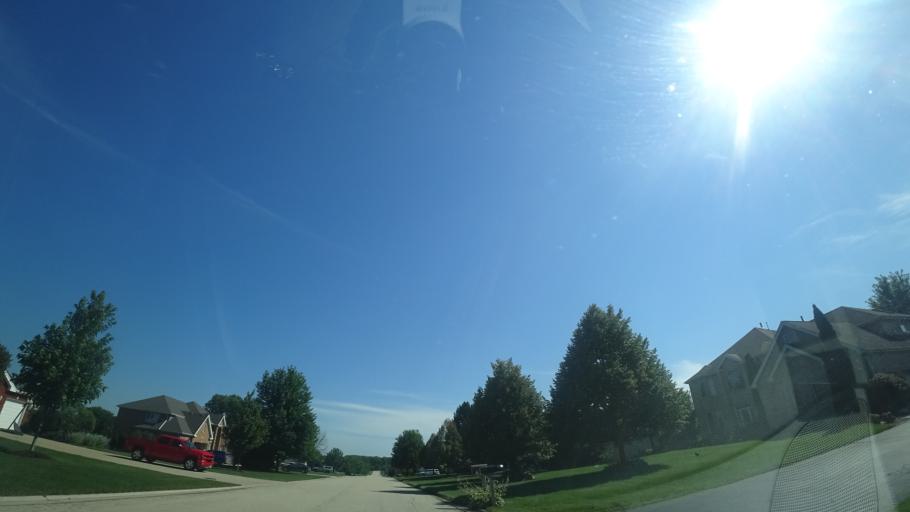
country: US
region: Illinois
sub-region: Will County
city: Homer Glen
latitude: 41.5634
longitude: -87.9180
